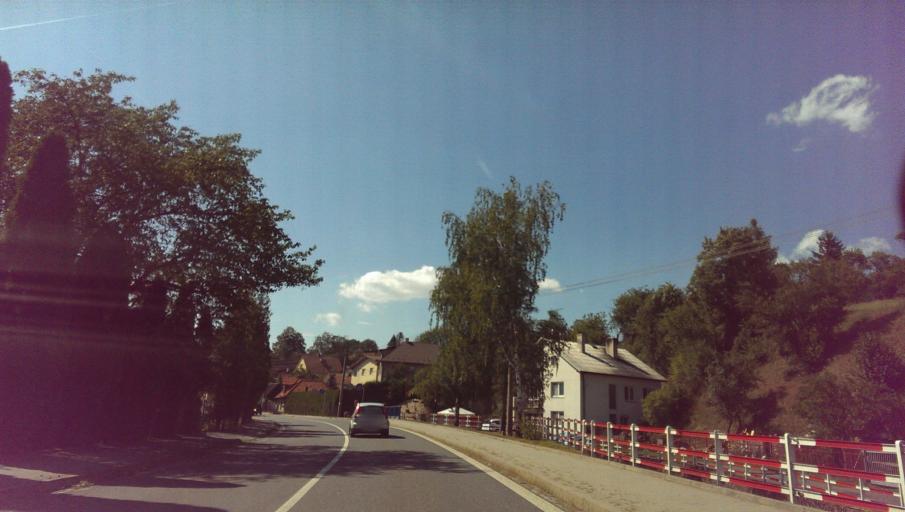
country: CZ
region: Zlin
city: Valasske Mezirici
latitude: 49.4668
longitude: 17.9450
